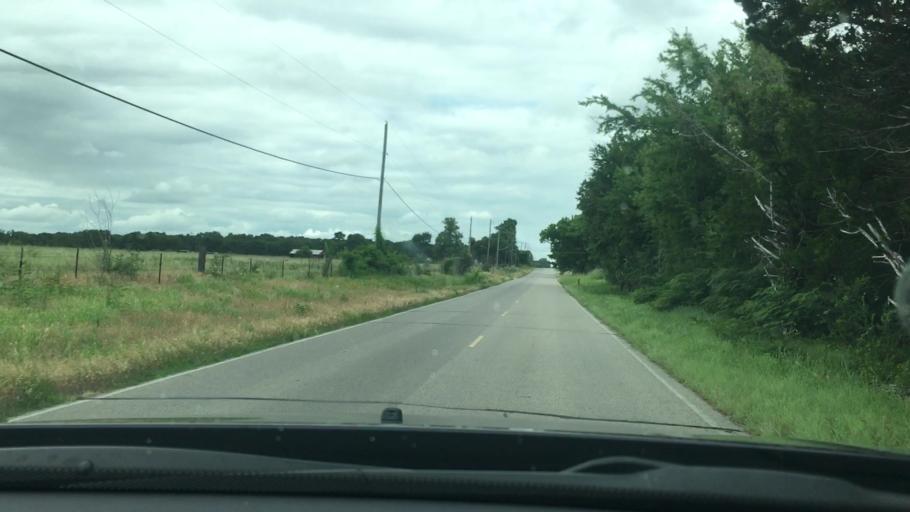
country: US
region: Oklahoma
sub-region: Carter County
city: Ardmore
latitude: 34.1365
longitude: -97.0731
